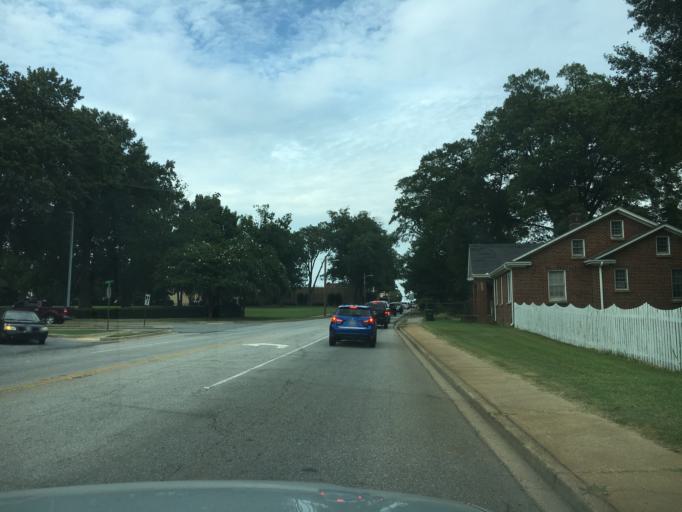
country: US
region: South Carolina
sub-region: Greenville County
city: Greer
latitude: 34.9361
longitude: -82.2296
